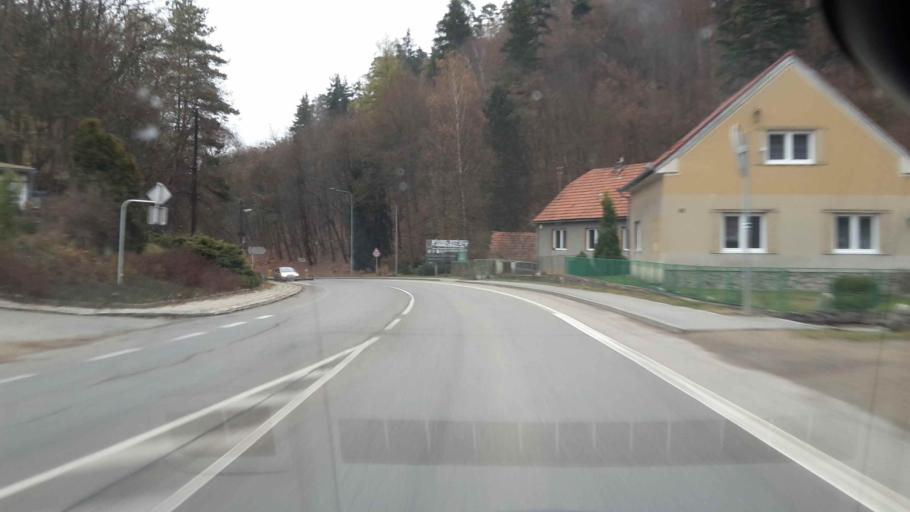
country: CZ
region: South Moravian
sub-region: Okres Brno-Venkov
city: Lelekovice
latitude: 49.3283
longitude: 16.6028
